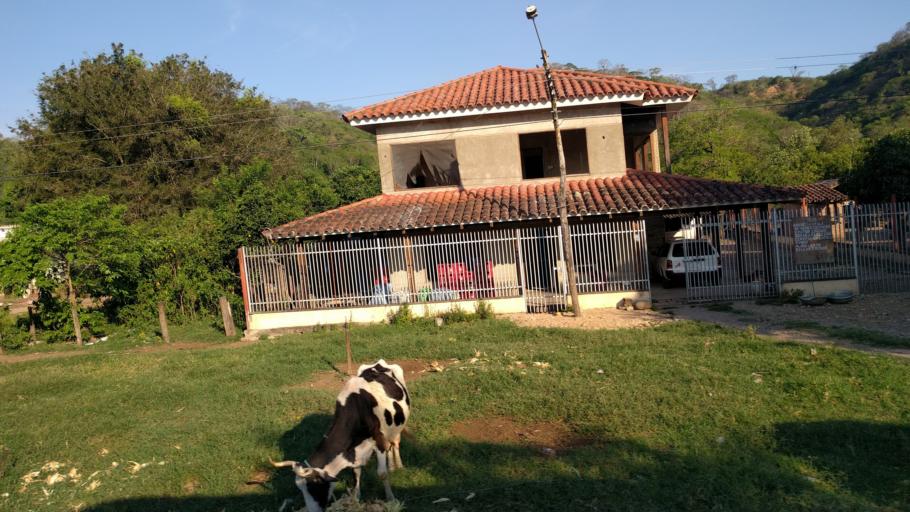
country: BO
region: Santa Cruz
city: Jorochito
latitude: -18.0762
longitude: -63.4451
